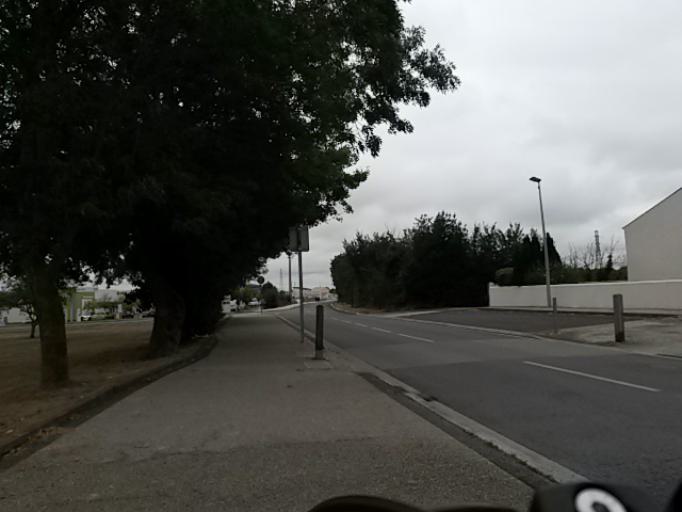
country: FR
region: Poitou-Charentes
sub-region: Departement de la Charente-Maritime
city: Saint-Xandre
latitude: 46.2058
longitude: -1.0948
